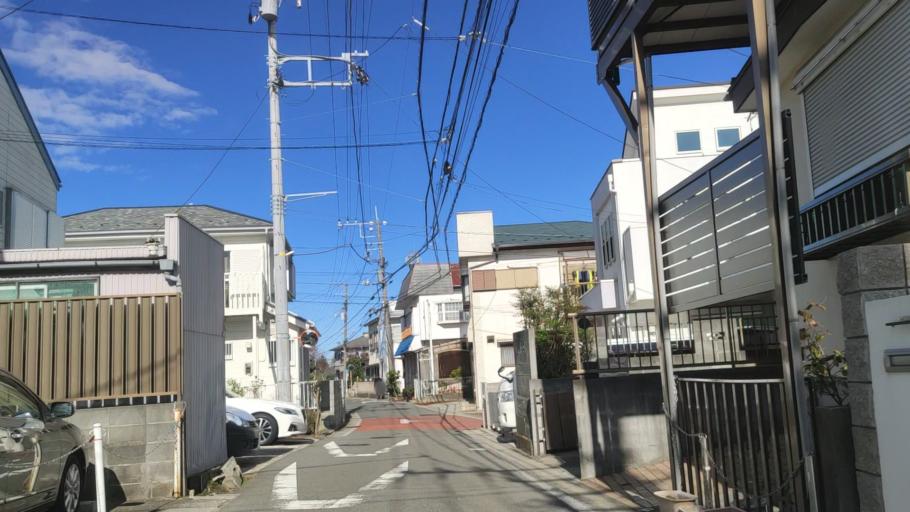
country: JP
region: Kanagawa
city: Yokohama
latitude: 35.4799
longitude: 139.5781
